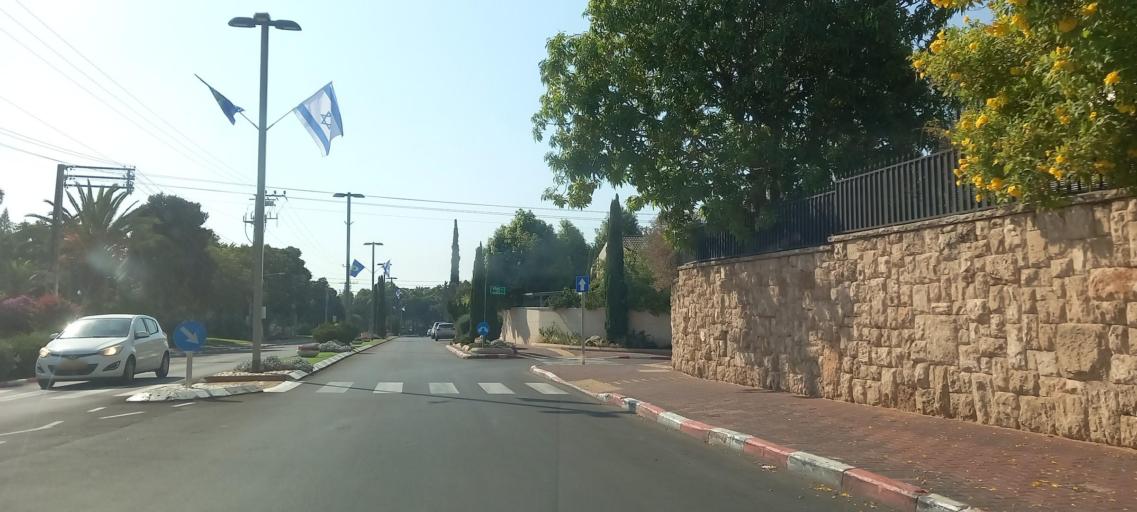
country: IL
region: Tel Aviv
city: Or Yehuda
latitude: 32.0486
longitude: 34.8358
